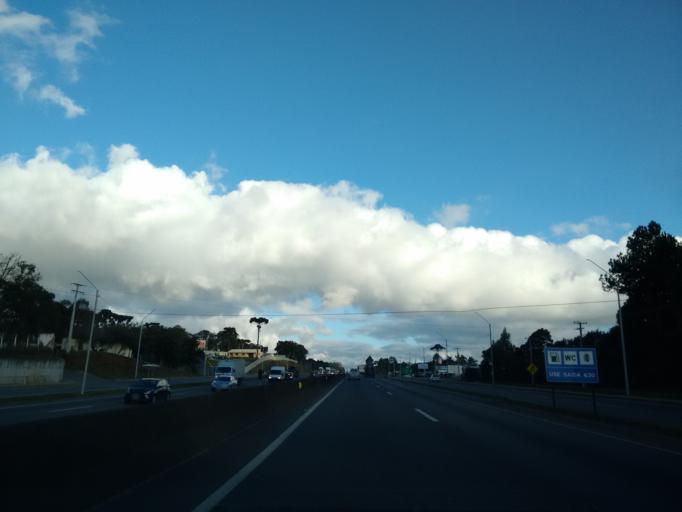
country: BR
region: Parana
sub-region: Sao Jose Dos Pinhais
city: Sao Jose dos Pinhais
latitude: -25.7052
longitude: -49.1417
